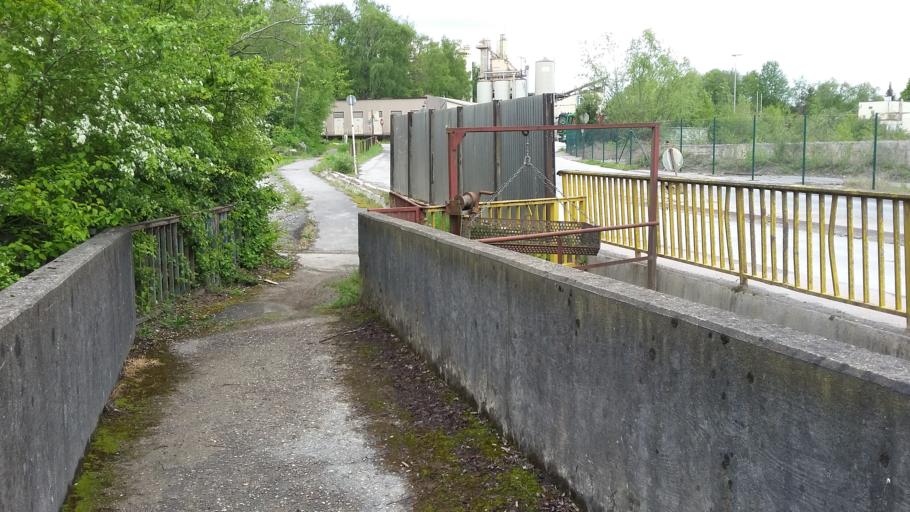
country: DE
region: North Rhine-Westphalia
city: Wulfrath
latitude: 51.2481
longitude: 7.0586
